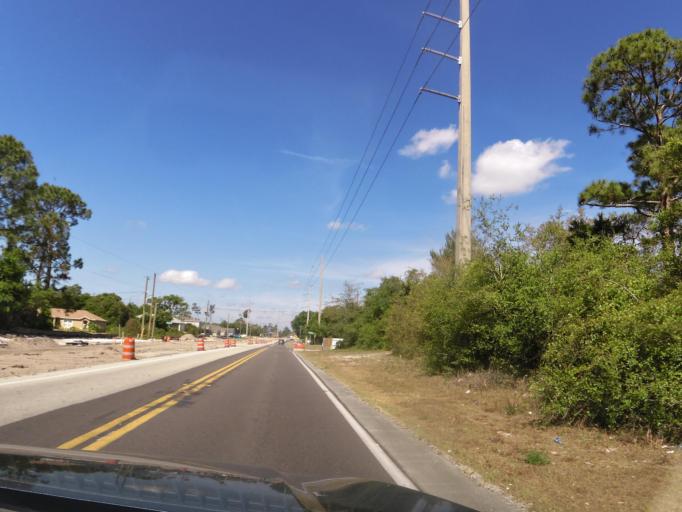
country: US
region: Florida
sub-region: Volusia County
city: Lake Helen
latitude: 28.9357
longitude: -81.2106
